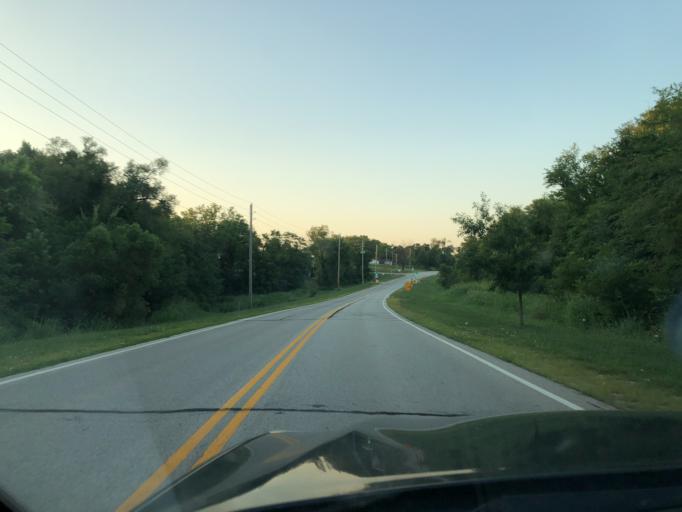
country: US
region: Kansas
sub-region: Leavenworth County
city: Leavenworth
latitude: 39.3336
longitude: -94.9165
